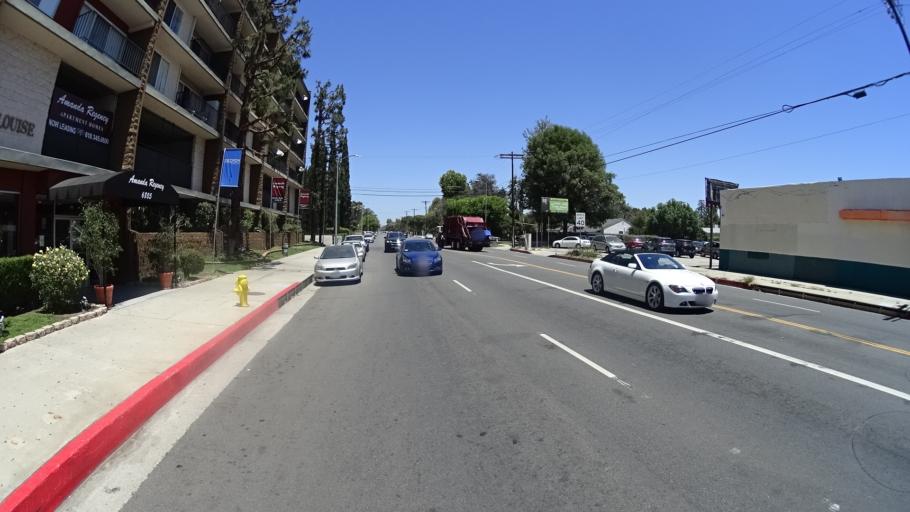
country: US
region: California
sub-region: Los Angeles County
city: Northridge
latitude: 34.1941
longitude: -118.5099
